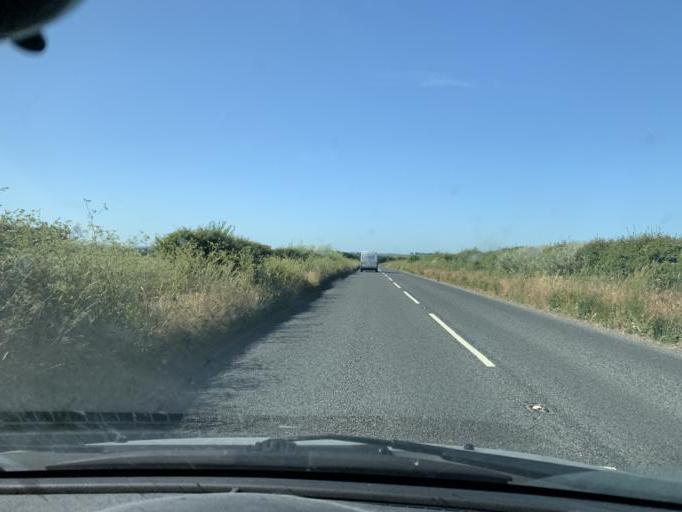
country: GB
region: England
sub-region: Wiltshire
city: Durnford
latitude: 51.1179
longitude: -1.7892
